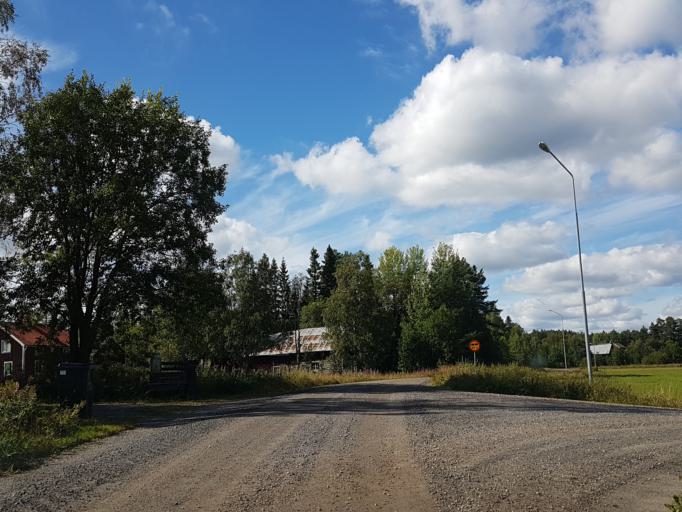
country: SE
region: Vaesterbotten
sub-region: Skelleftea Kommun
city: Burtraesk
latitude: 64.2910
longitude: 20.4540
